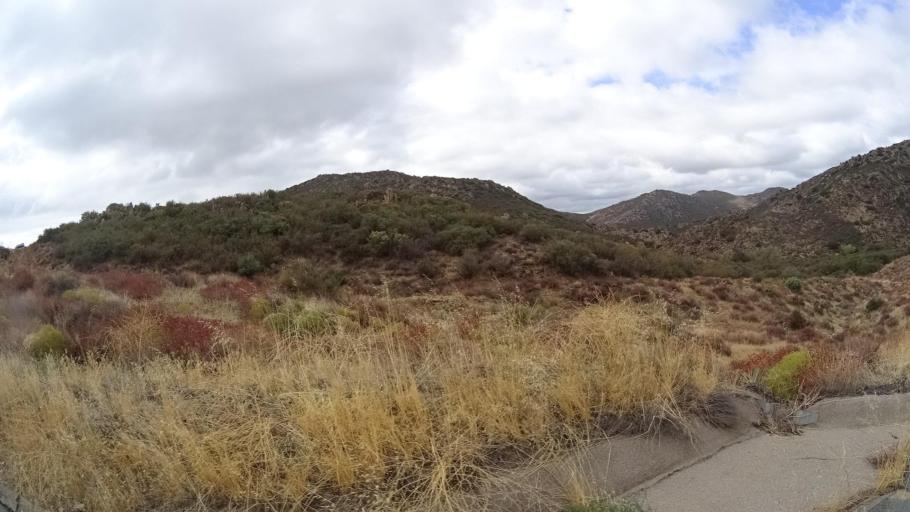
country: US
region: California
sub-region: San Diego County
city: Pine Valley
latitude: 32.7495
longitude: -116.4508
